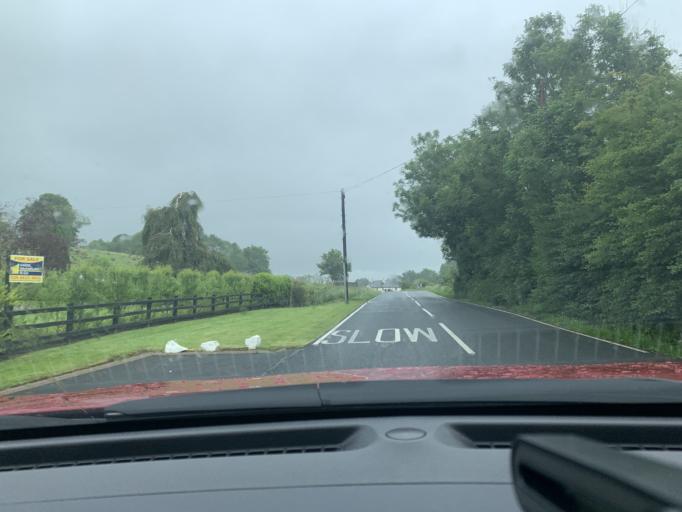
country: GB
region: Northern Ireland
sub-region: Fermanagh District
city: Enniskillen
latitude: 54.2991
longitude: -7.6925
